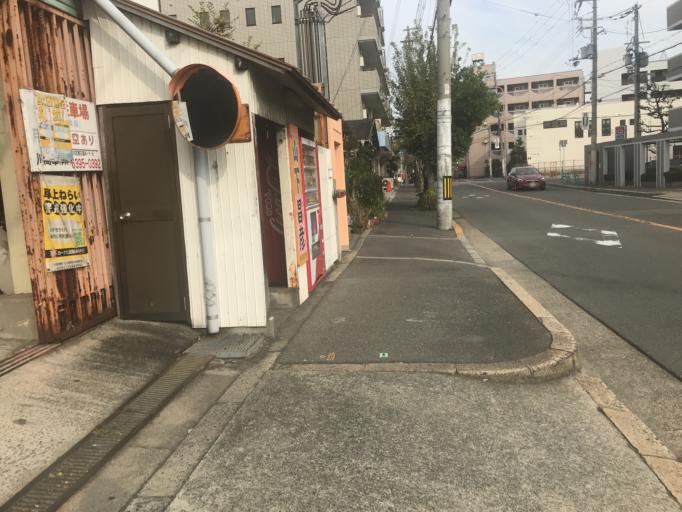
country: JP
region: Osaka
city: Suita
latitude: 34.7432
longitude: 135.4883
